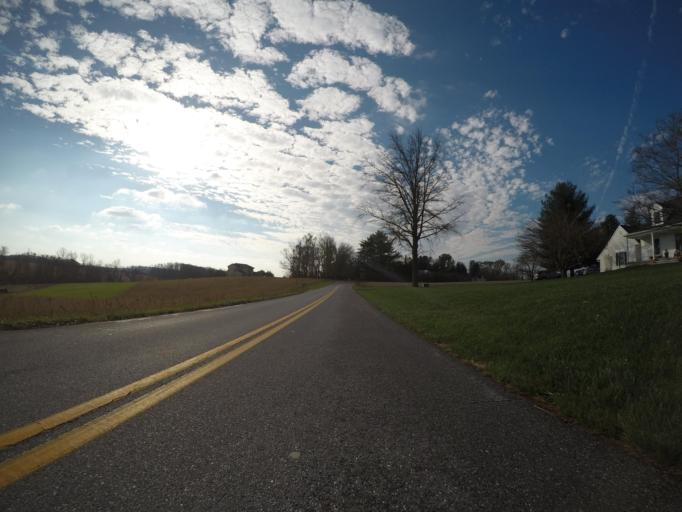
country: US
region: Maryland
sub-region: Carroll County
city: Hampstead
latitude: 39.5820
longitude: -76.8044
